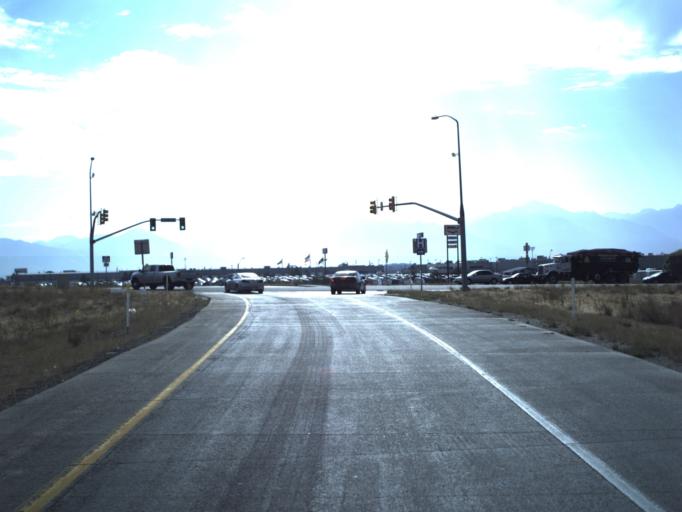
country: US
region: Utah
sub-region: Salt Lake County
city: West Valley City
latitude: 40.7248
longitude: -112.0258
